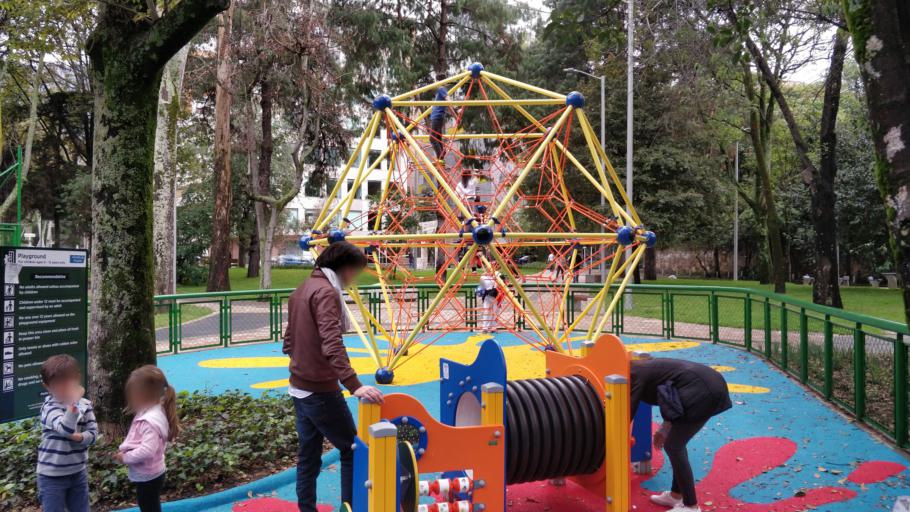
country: CO
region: Bogota D.C.
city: Barrio San Luis
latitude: 4.6703
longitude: -74.0506
